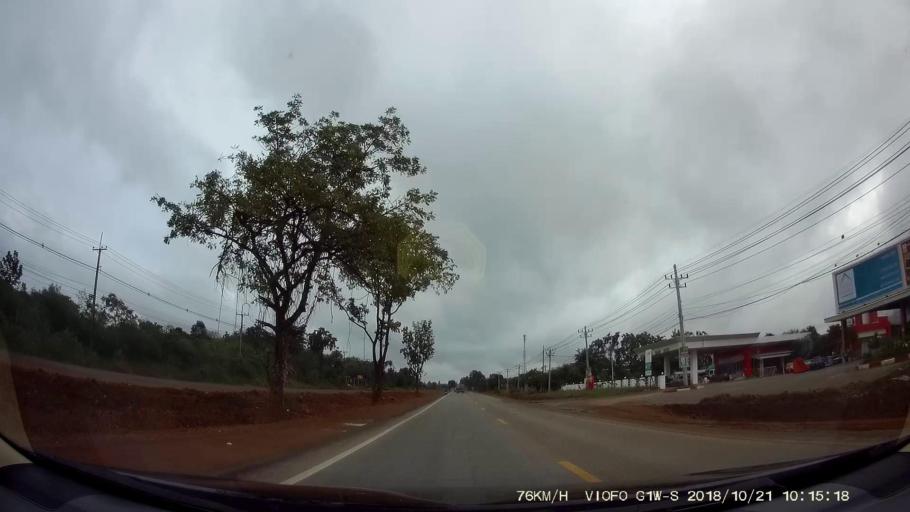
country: TH
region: Chaiyaphum
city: Phu Khiao
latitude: 16.3422
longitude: 102.1641
